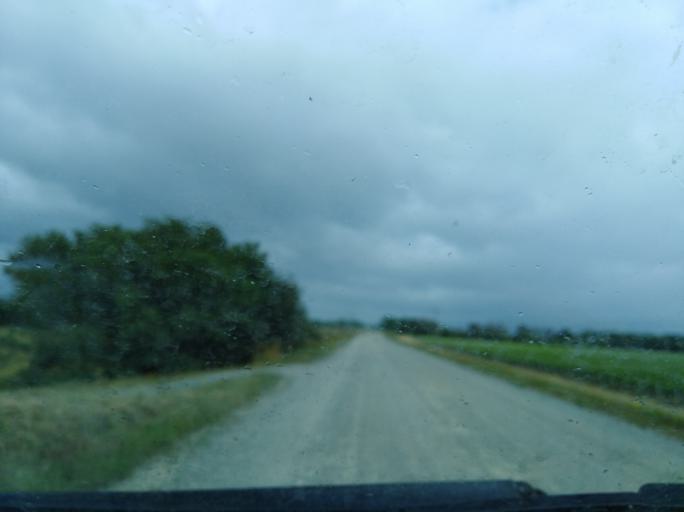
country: NZ
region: Marlborough
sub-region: Marlborough District
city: Blenheim
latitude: -41.4407
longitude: 174.0098
